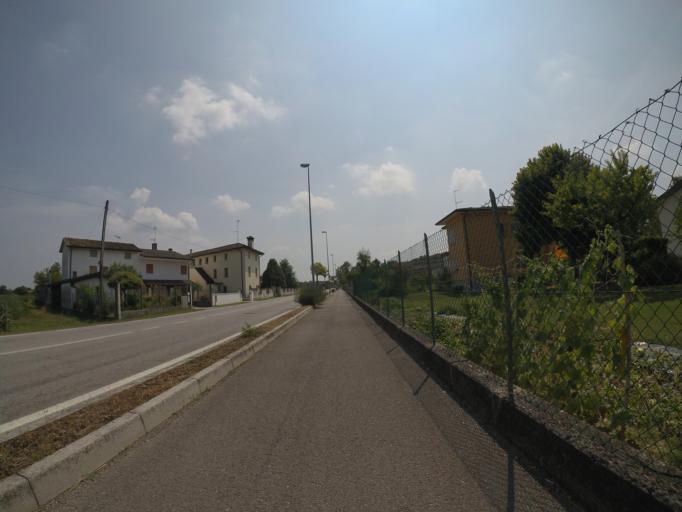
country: IT
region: Friuli Venezia Giulia
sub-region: Provincia di Udine
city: Teor
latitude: 45.8607
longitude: 13.0520
